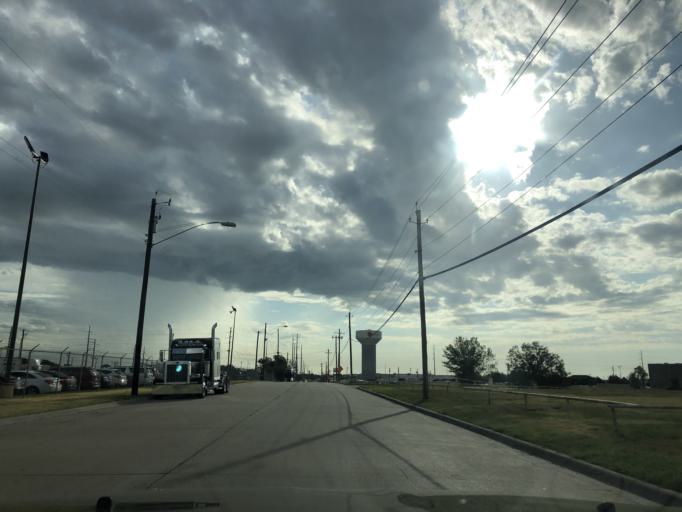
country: US
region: Texas
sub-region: Dallas County
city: Garland
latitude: 32.8716
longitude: -96.6701
